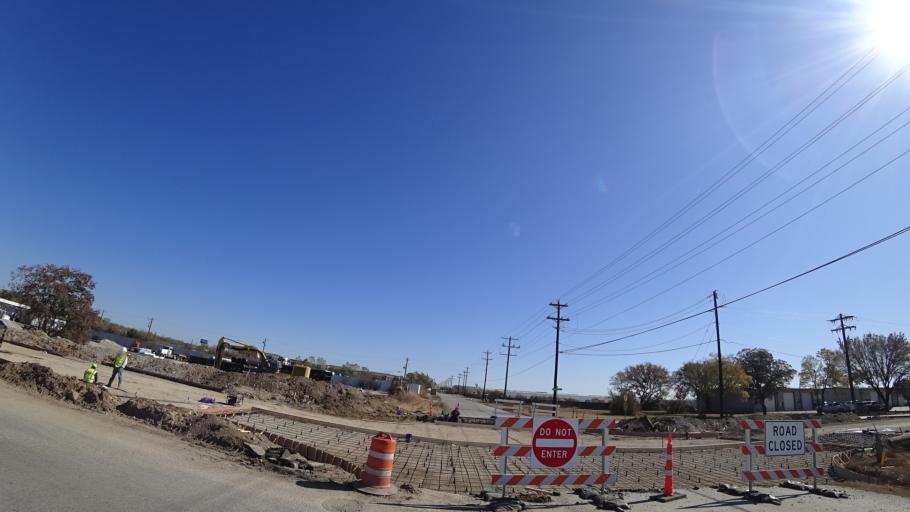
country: US
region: Texas
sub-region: Denton County
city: Lewisville
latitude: 33.0468
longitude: -96.9368
